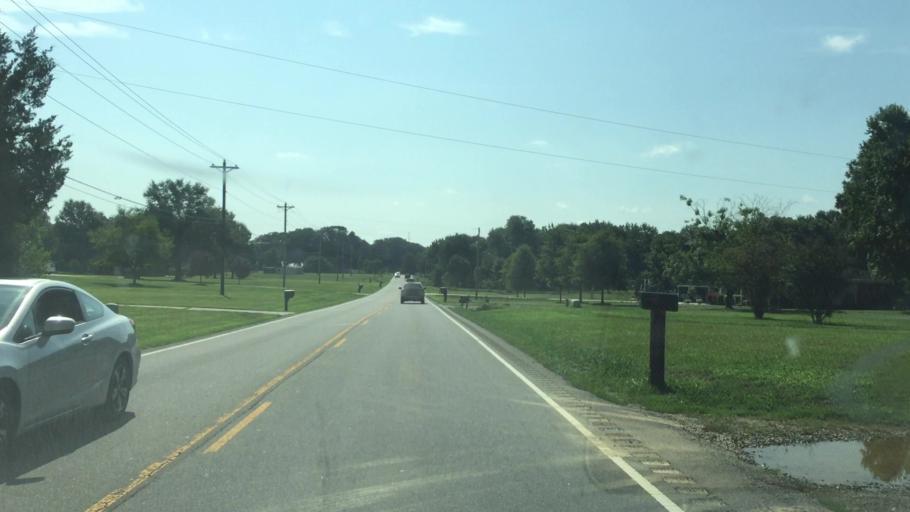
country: US
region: North Carolina
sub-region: Union County
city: Fairview
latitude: 35.1529
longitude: -80.5583
